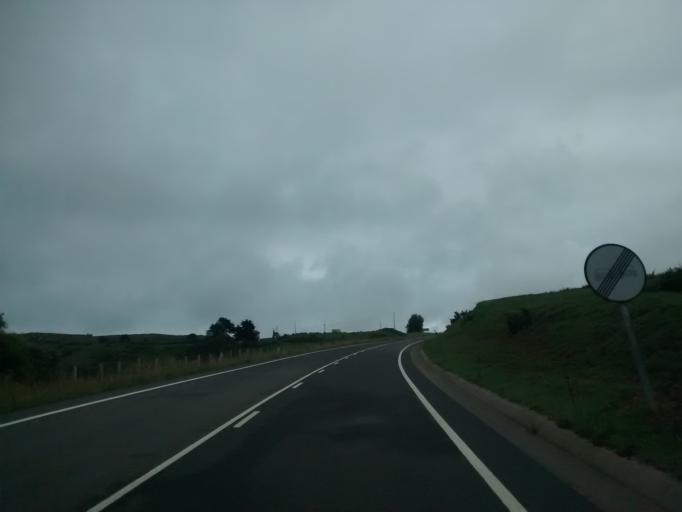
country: ES
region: Cantabria
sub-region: Provincia de Cantabria
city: Santillana
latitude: 43.3980
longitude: -4.1132
